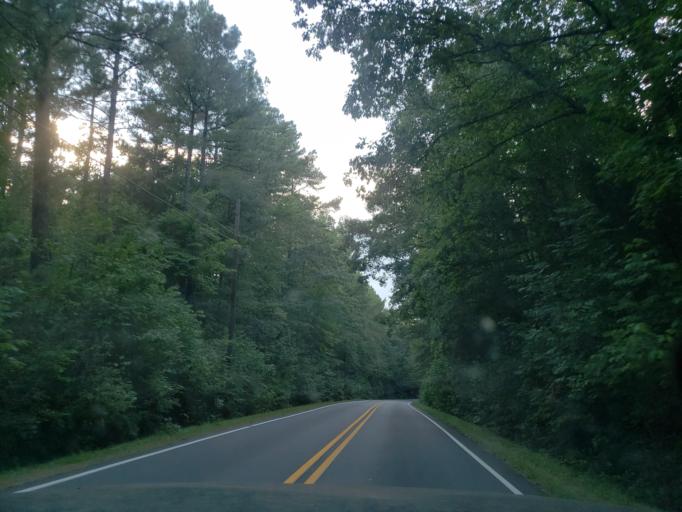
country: US
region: North Carolina
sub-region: Durham County
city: Durham
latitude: 35.9904
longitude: -78.9694
